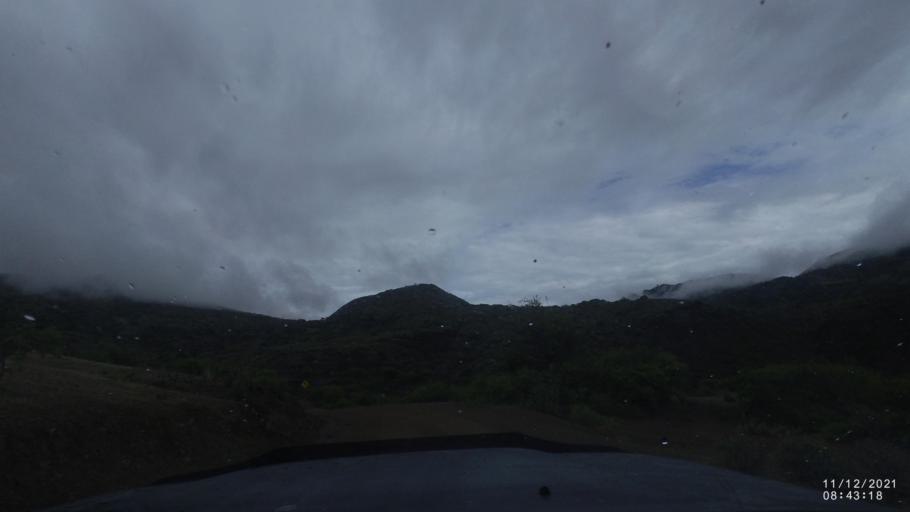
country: BO
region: Cochabamba
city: Tarata
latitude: -17.9138
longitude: -65.9365
